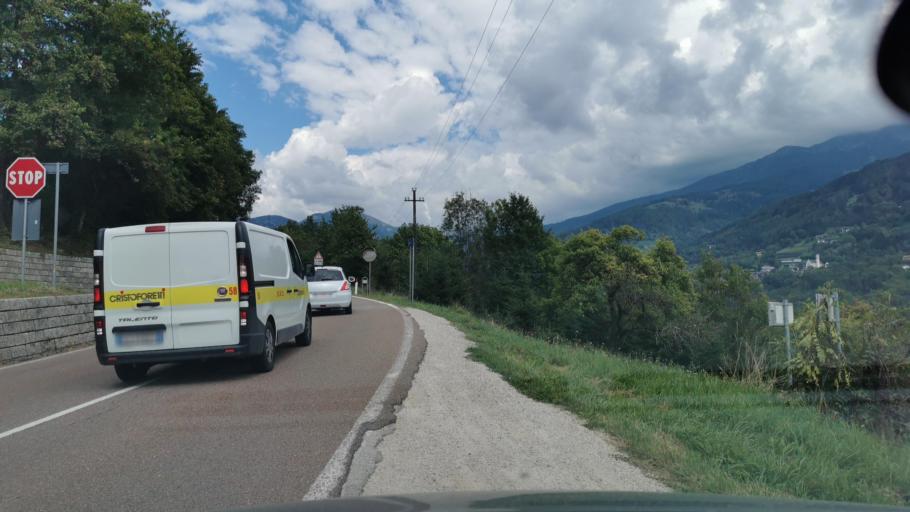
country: IT
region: Trentino-Alto Adige
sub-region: Provincia di Trento
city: Frassilongo
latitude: 46.0857
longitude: 11.2772
